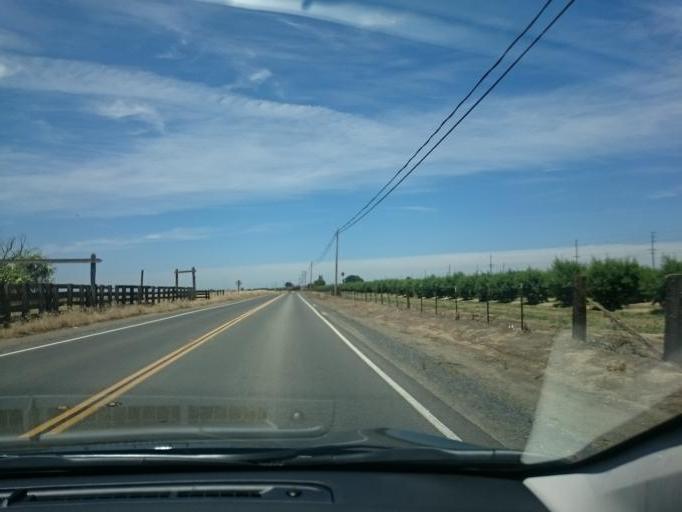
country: US
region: California
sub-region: Stanislaus County
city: Waterford
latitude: 37.6465
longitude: -120.6773
